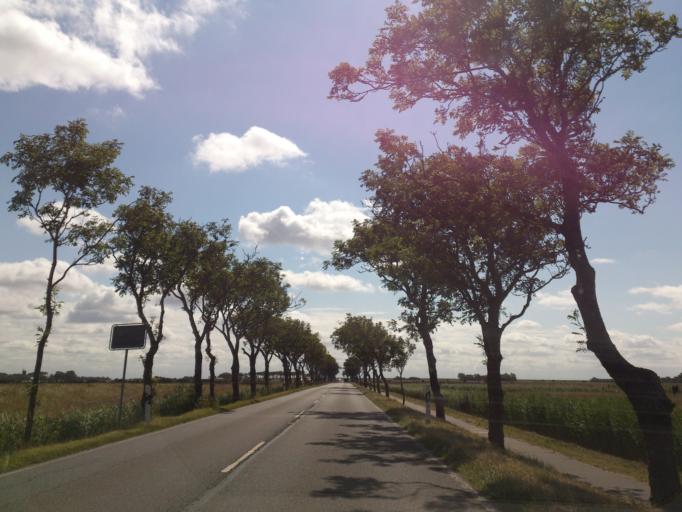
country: DE
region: Schleswig-Holstein
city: Sankt Peter-Ording
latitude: 54.3016
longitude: 8.6764
